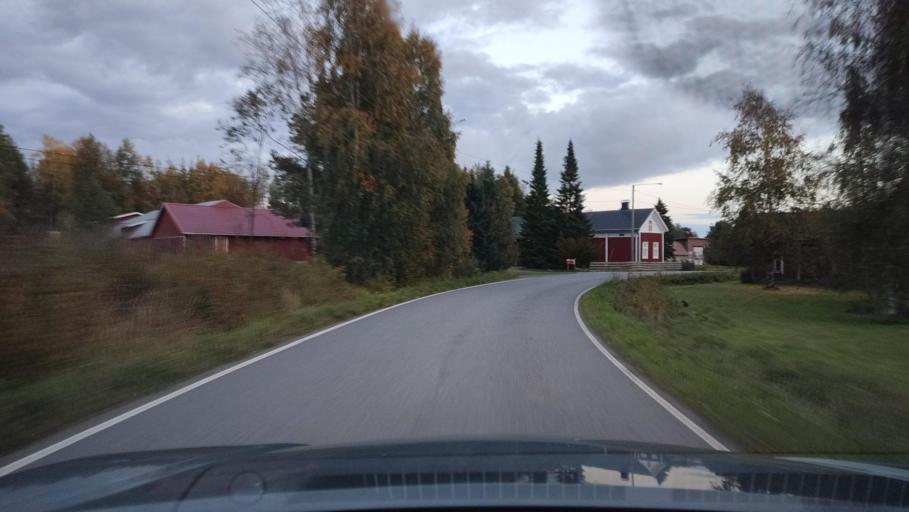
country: FI
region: Ostrobothnia
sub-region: Sydosterbotten
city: Kristinestad
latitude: 62.2642
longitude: 21.5281
